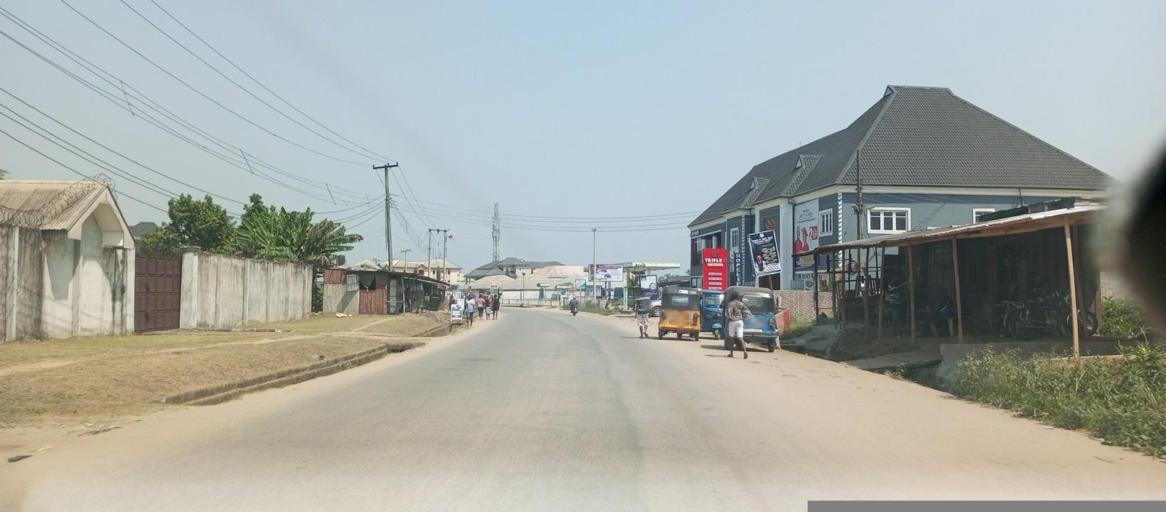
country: NG
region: Rivers
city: Emuoha
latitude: 4.9160
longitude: 6.9162
